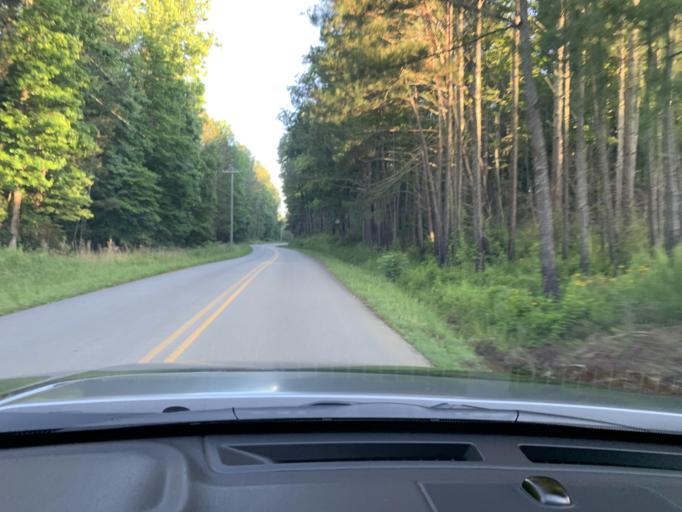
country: US
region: Georgia
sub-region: Bartow County
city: Rydal
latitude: 34.2546
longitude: -84.6897
